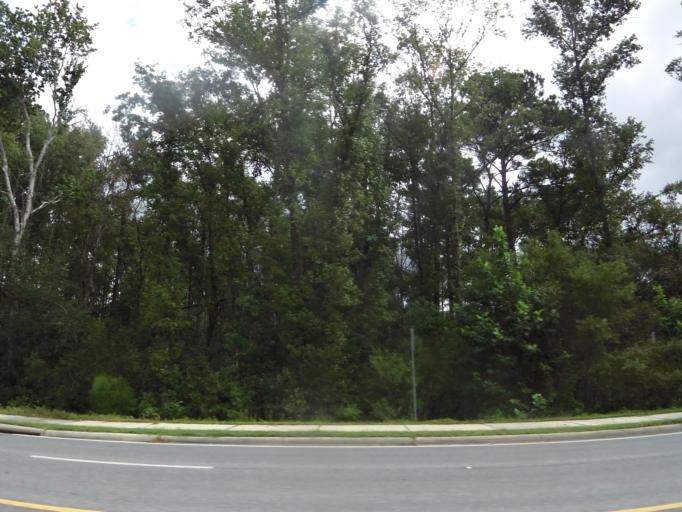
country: US
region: Florida
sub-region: Clay County
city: Asbury Lake
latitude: 30.0897
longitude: -81.8098
